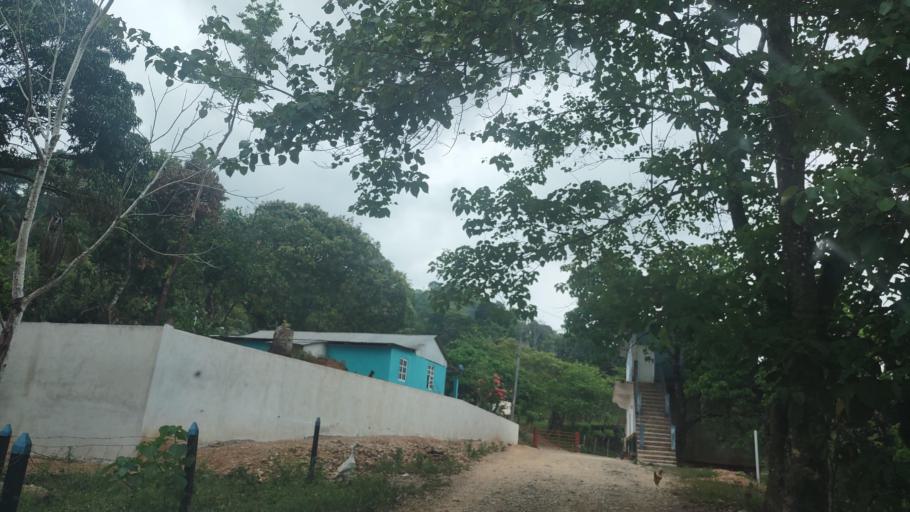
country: MX
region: Tabasco
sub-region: Huimanguillo
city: Francisco Rueda
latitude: 17.4432
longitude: -94.0243
